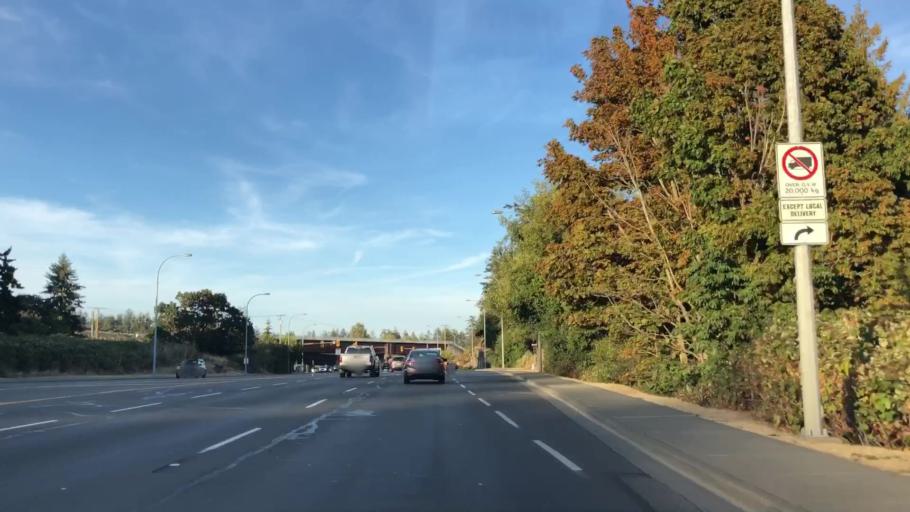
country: CA
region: British Columbia
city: Colwood
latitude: 48.4595
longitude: -123.4566
